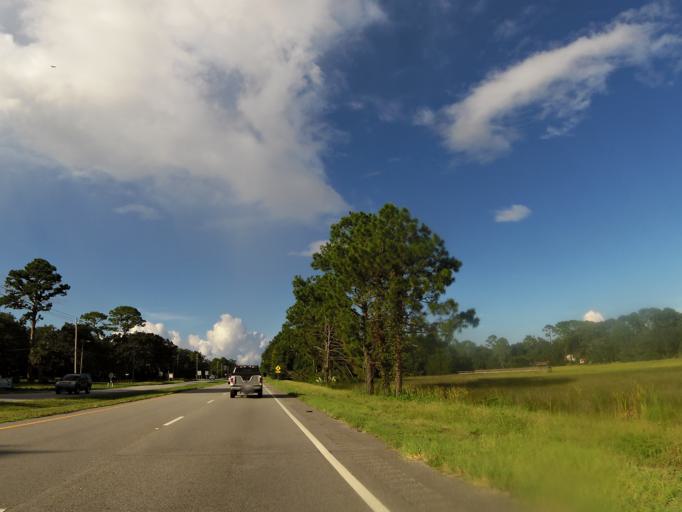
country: US
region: Georgia
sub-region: Glynn County
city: Country Club Estates
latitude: 31.2150
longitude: -81.4652
